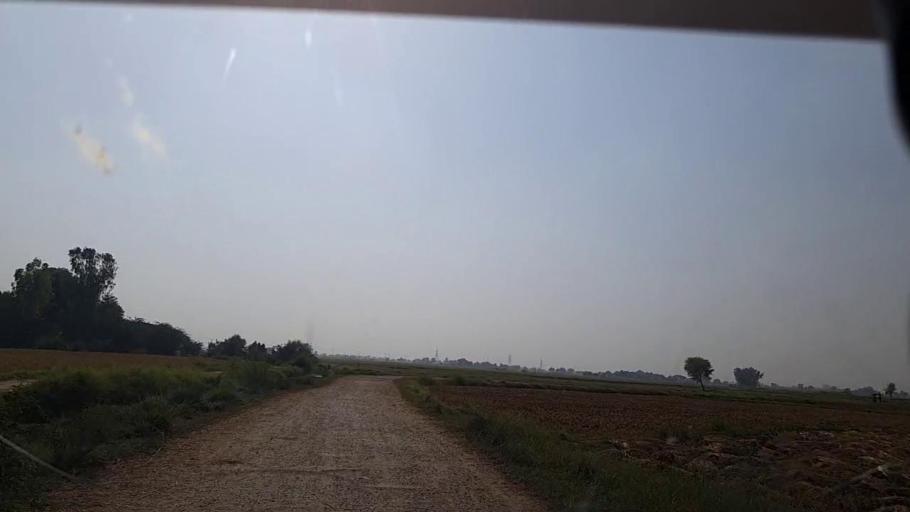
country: PK
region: Sindh
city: Shikarpur
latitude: 28.0914
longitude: 68.6021
